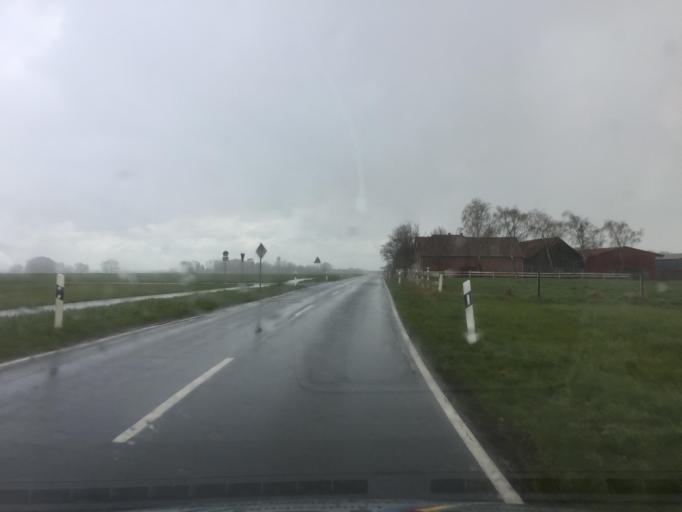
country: DE
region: Lower Saxony
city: Sustedt
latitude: 52.9217
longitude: 8.8905
